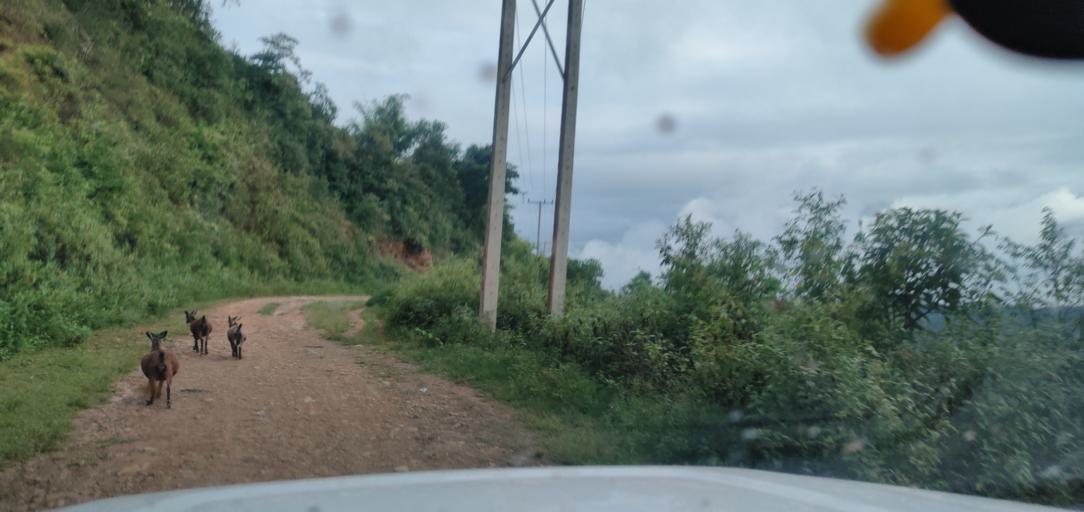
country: LA
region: Phongsali
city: Phongsali
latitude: 21.4434
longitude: 102.2937
